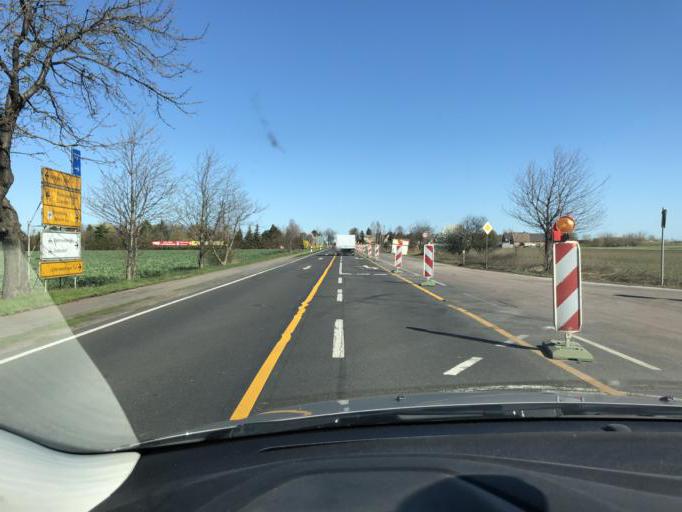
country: DE
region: Saxony-Anhalt
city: Welsleben
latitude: 52.0544
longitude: 11.6135
